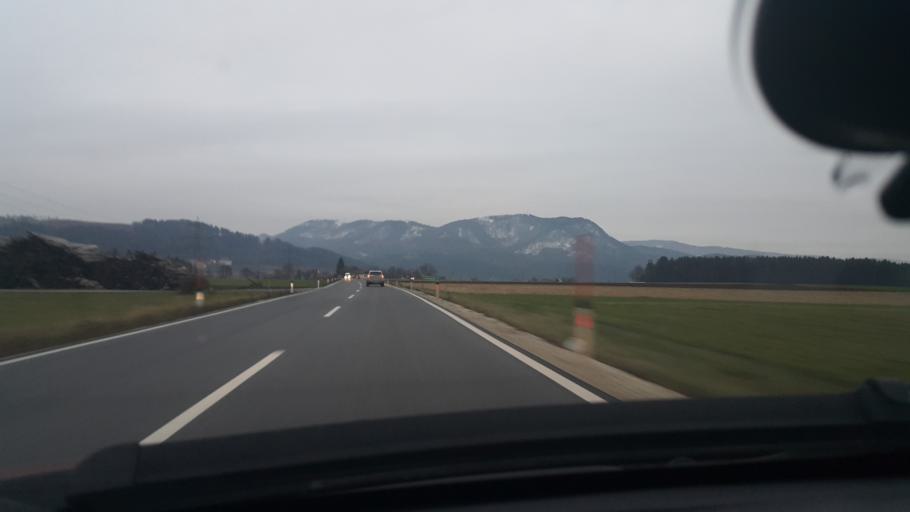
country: AT
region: Carinthia
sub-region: Politischer Bezirk Volkermarkt
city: Griffen
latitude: 46.6908
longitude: 14.7426
